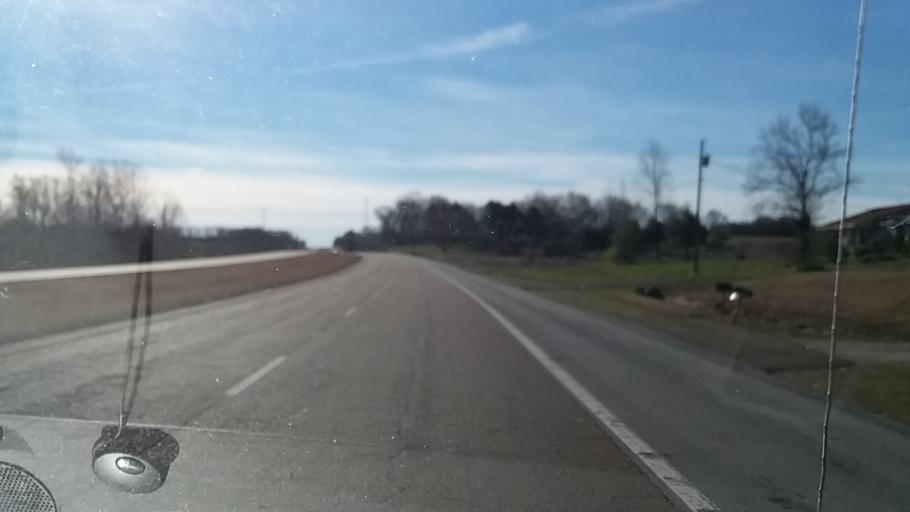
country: US
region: Tennessee
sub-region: Lauderdale County
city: Halls
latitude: 35.9182
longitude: -89.2737
